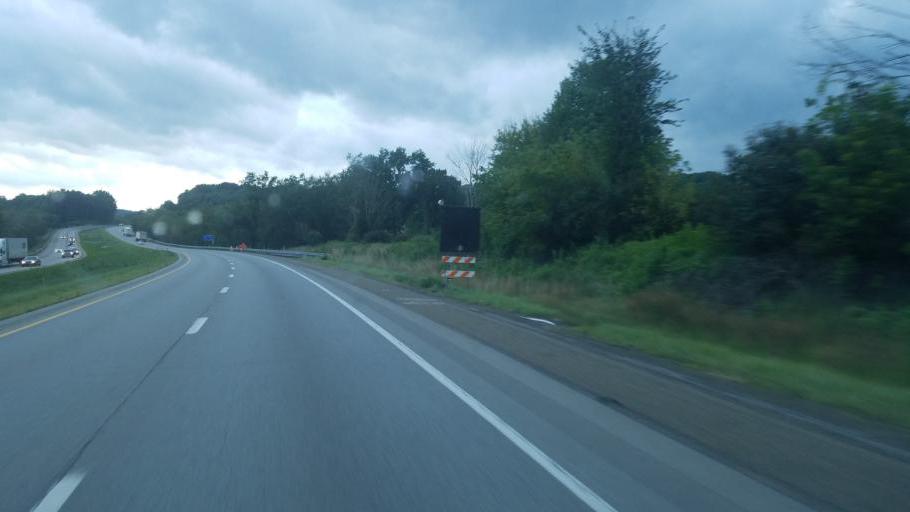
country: US
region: Pennsylvania
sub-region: Butler County
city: Zelienople
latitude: 40.8215
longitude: -80.1053
